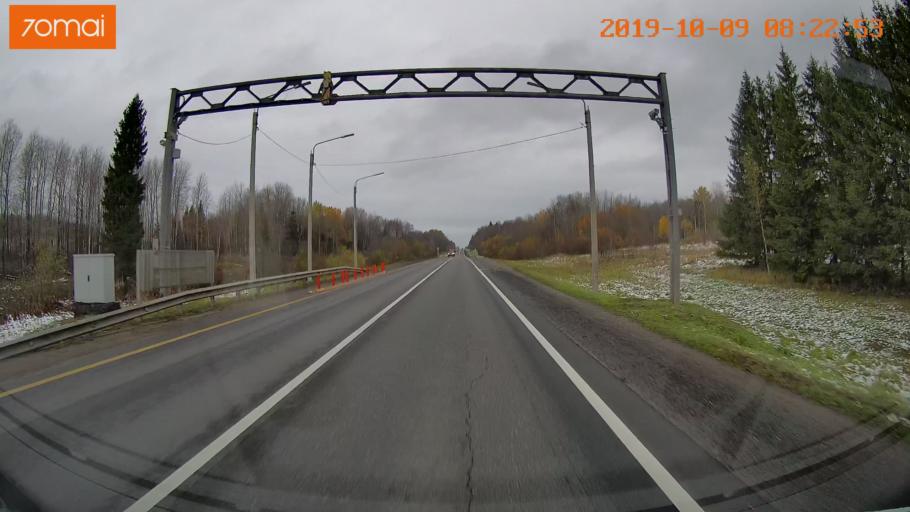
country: RU
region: Vologda
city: Gryazovets
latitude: 58.7474
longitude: 40.2863
